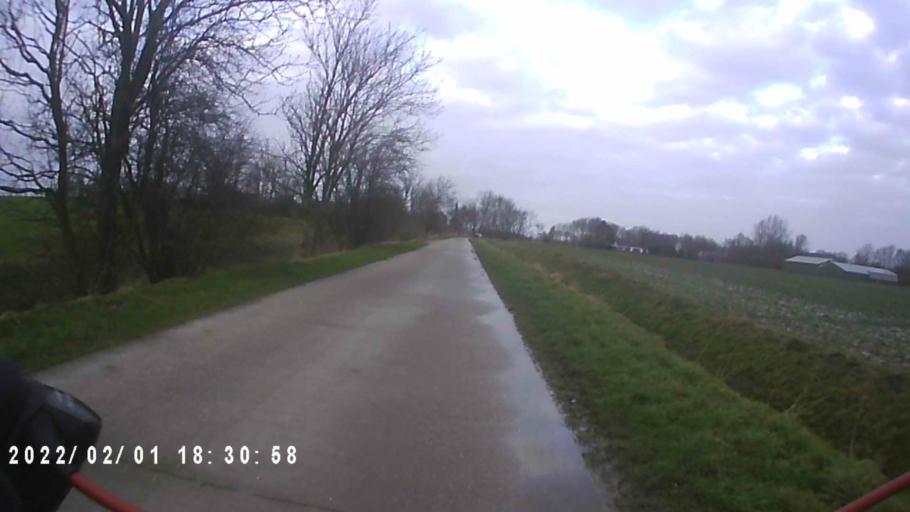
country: NL
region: Groningen
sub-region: Gemeente De Marne
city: Ulrum
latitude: 53.3571
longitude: 6.3198
